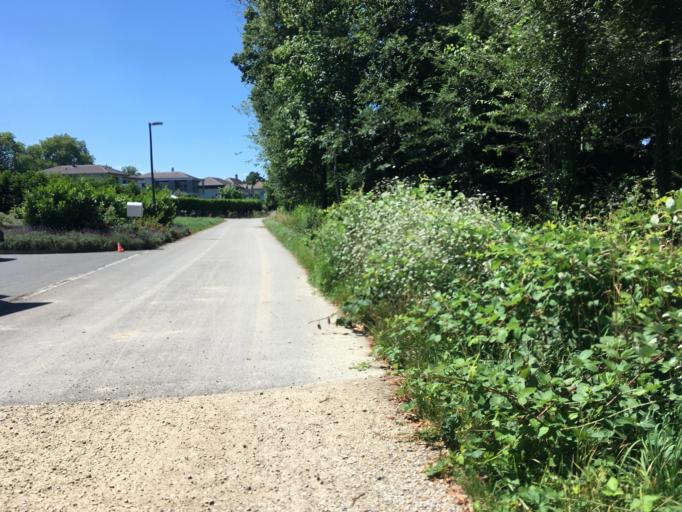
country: CH
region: Fribourg
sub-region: See District
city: Gurwolf
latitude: 46.9174
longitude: 7.0901
